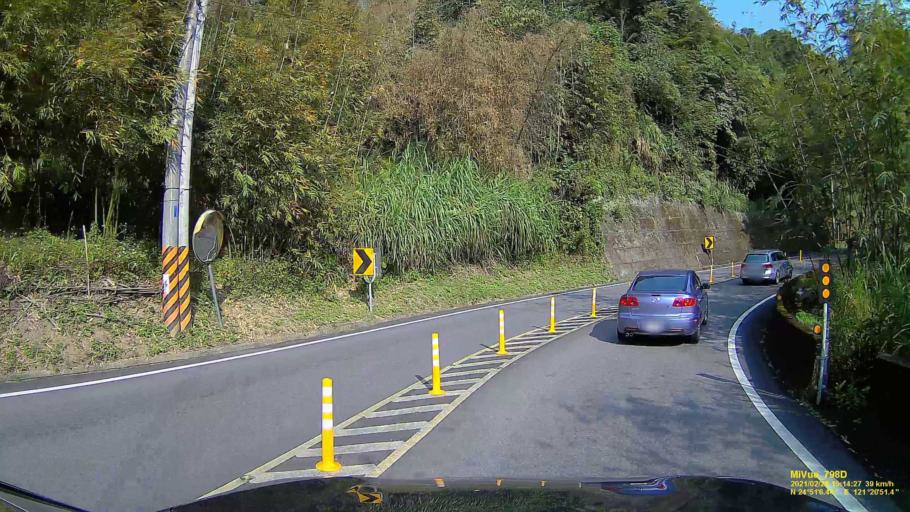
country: TW
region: Taiwan
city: Daxi
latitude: 24.8516
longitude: 121.3478
